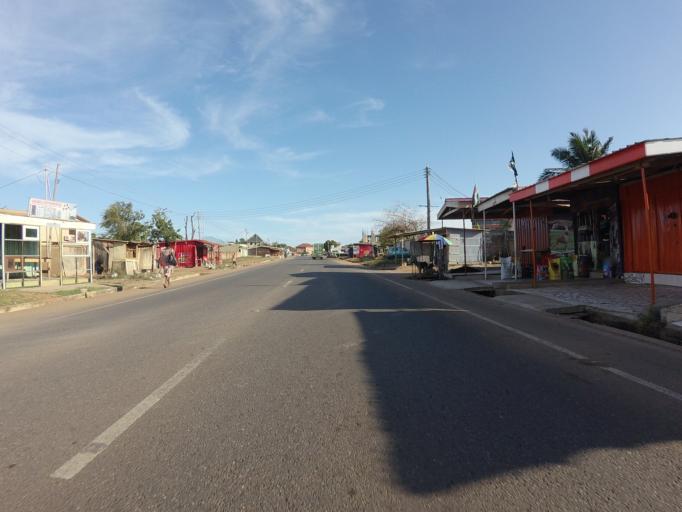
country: GH
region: Greater Accra
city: Nungua
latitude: 5.6360
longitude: -0.0915
